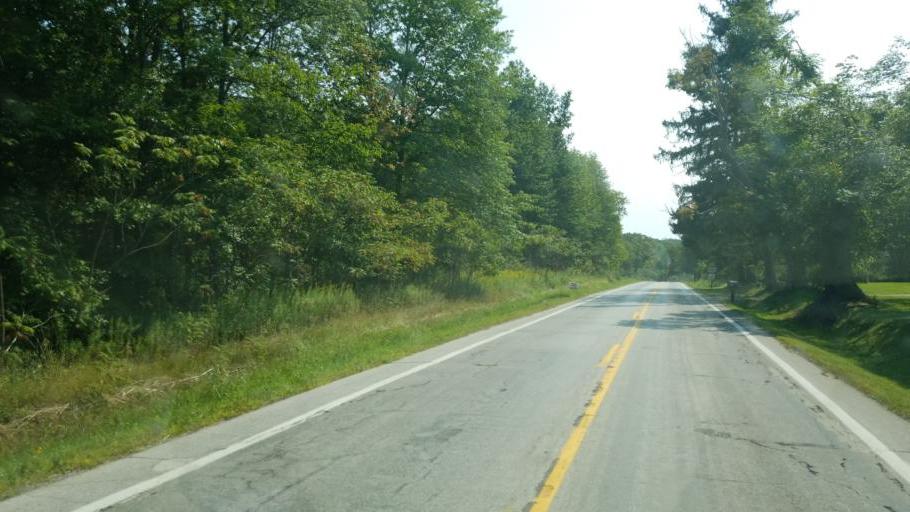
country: US
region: Ohio
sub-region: Ashtabula County
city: Orwell
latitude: 41.5459
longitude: -80.9492
